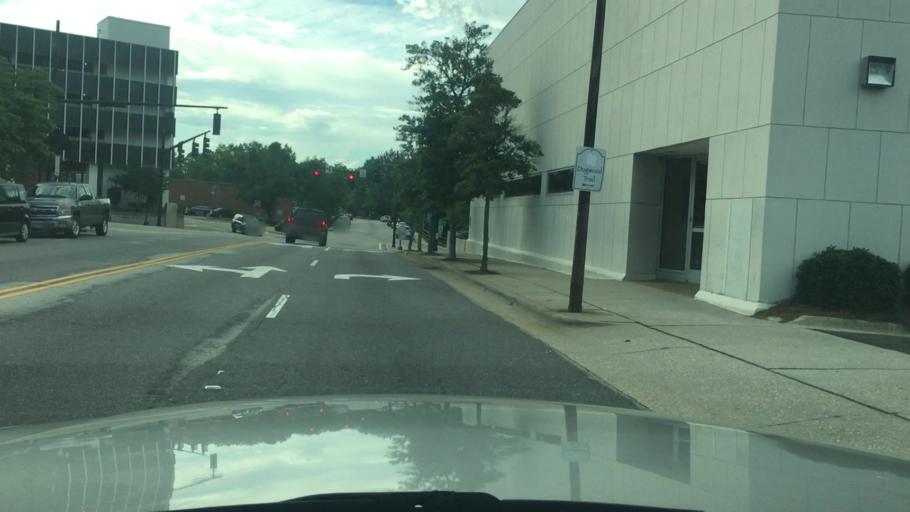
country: US
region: North Carolina
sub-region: Cumberland County
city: Fayetteville
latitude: 35.0532
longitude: -78.8774
